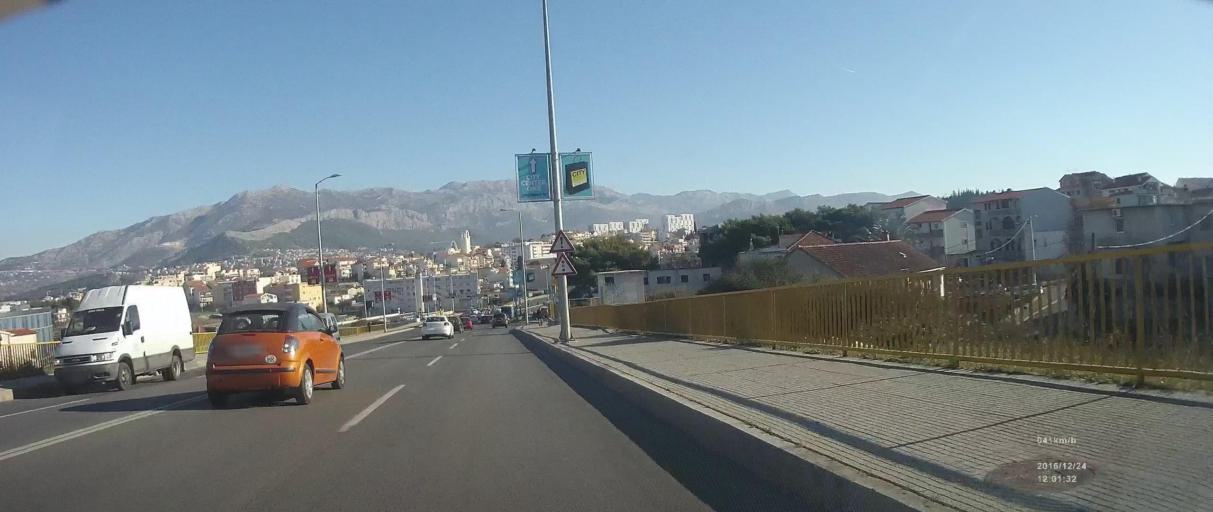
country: HR
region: Splitsko-Dalmatinska
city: Vranjic
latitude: 43.5164
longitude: 16.4833
